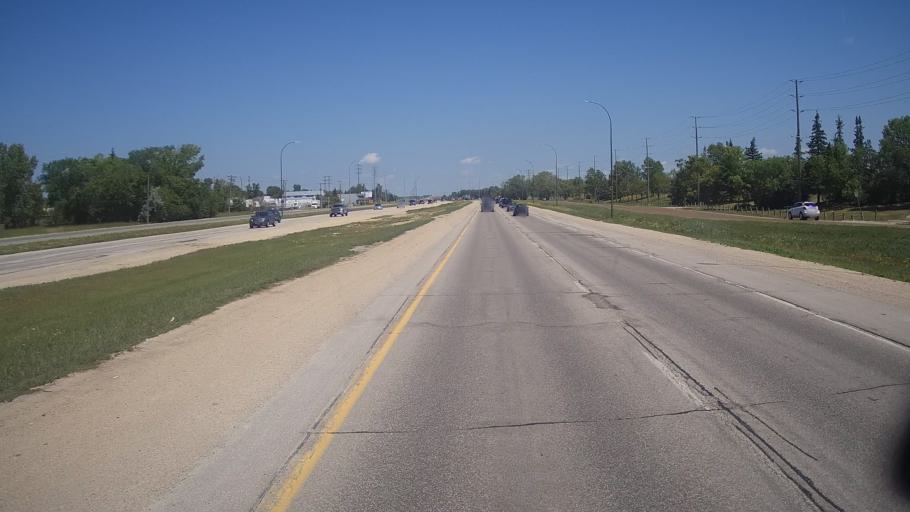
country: CA
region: Manitoba
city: Winnipeg
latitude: 49.9319
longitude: -97.0437
